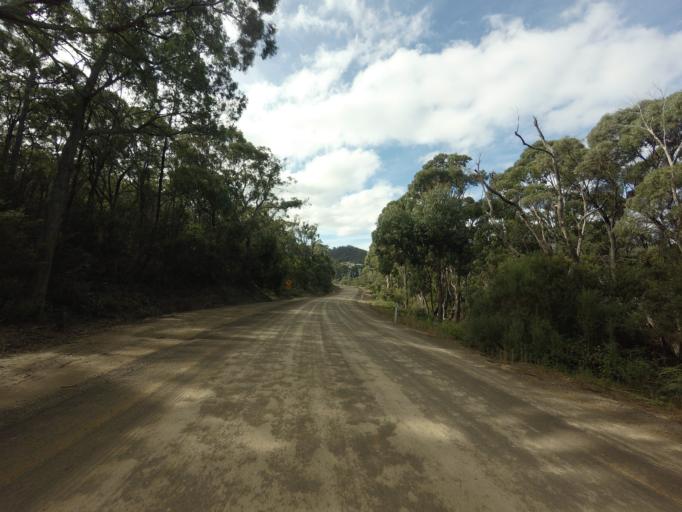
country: AU
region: Tasmania
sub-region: Clarence
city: Sandford
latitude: -43.0934
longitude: 147.7289
